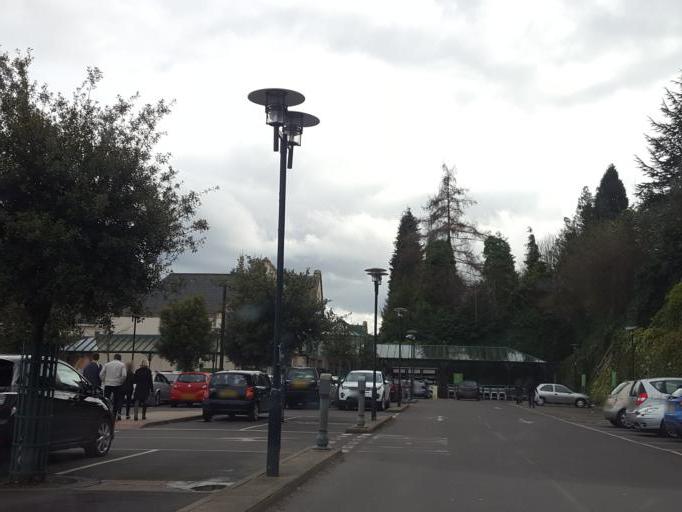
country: GB
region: England
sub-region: Worcestershire
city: Great Malvern
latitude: 52.1136
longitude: -2.3290
